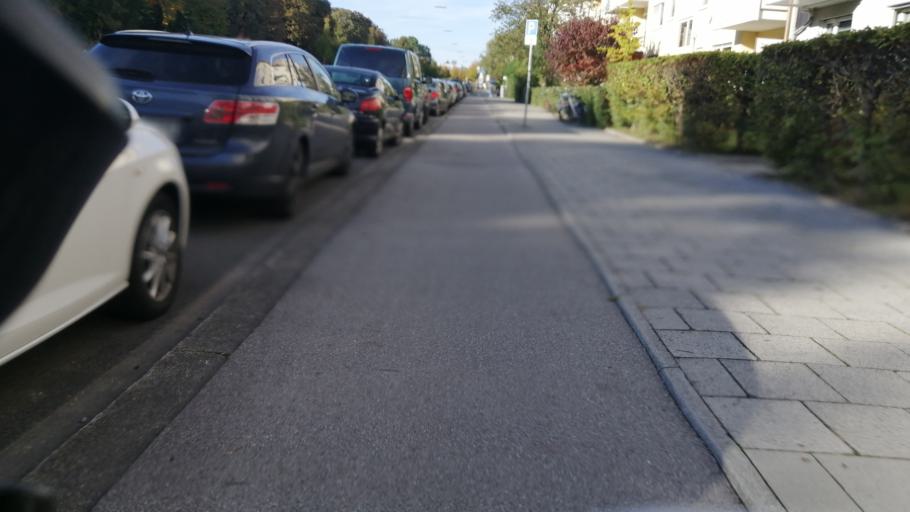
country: DE
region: Bavaria
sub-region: Upper Bavaria
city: Munich
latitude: 48.1743
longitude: 11.5732
